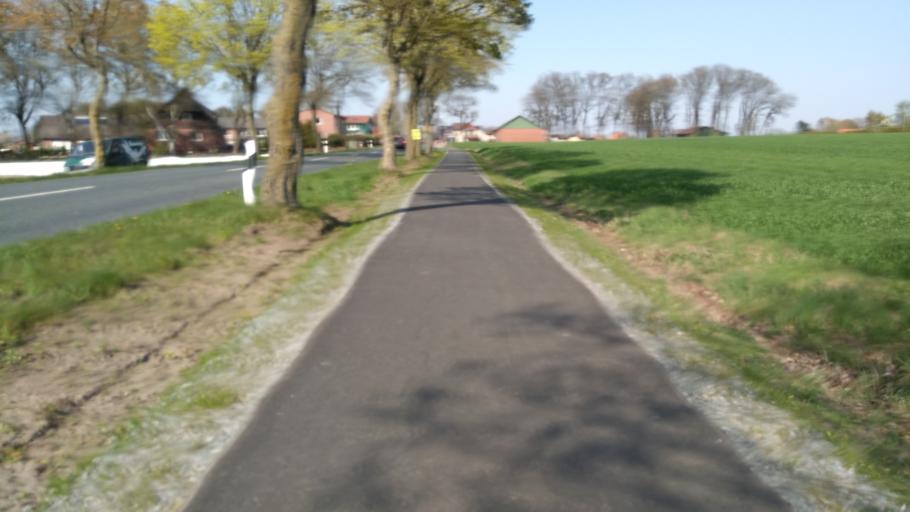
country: DE
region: Lower Saxony
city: Bliedersdorf
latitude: 53.4765
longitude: 9.5651
